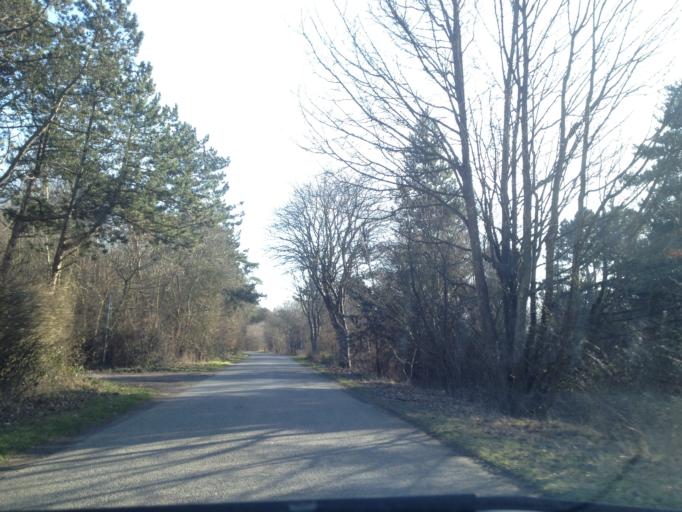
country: DK
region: South Denmark
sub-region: Kerteminde Kommune
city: Munkebo
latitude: 55.5548
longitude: 10.6150
